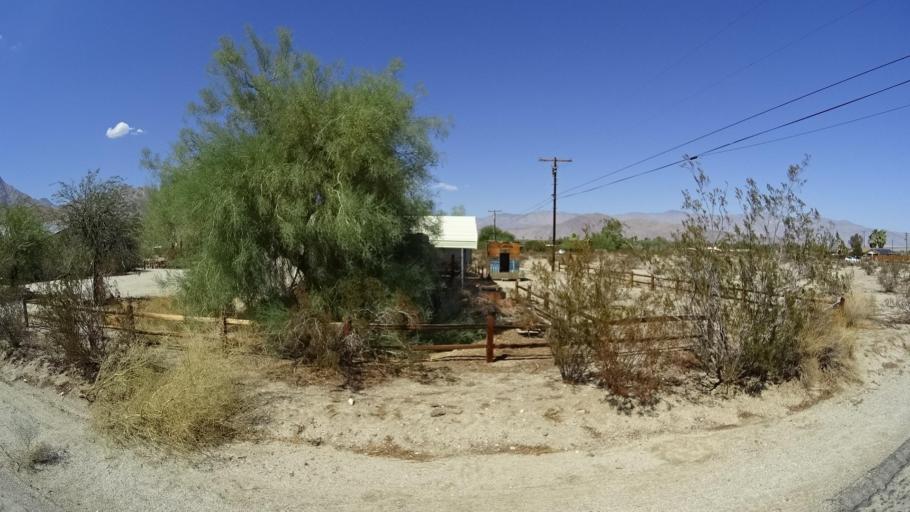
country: US
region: California
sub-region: San Diego County
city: Borrego Springs
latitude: 33.2407
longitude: -116.3753
